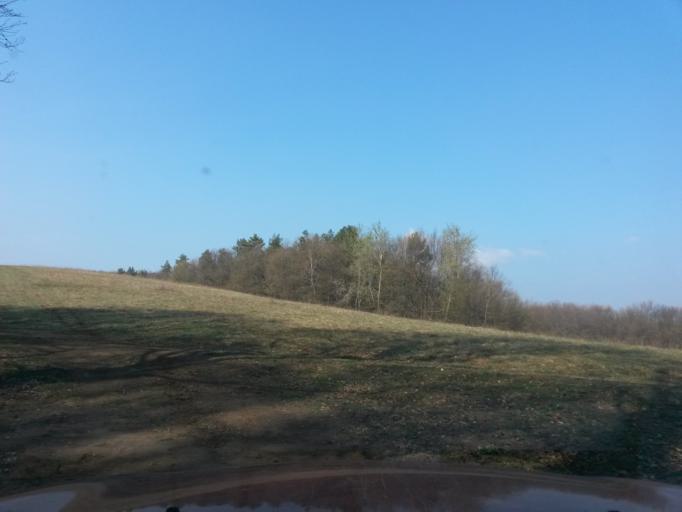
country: SK
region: Presovsky
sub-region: Okres Presov
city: Presov
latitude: 48.9294
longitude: 21.1530
